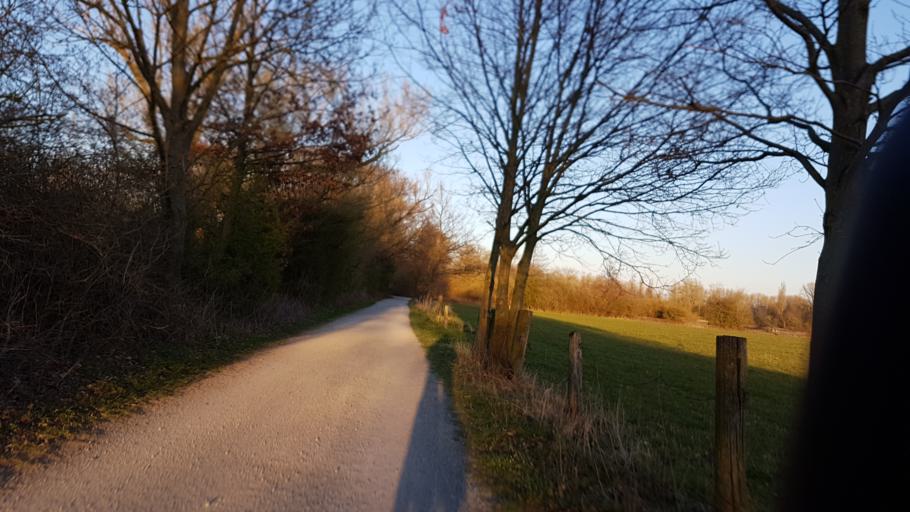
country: DE
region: Lower Saxony
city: Laatzen
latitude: 52.3142
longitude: 9.7691
